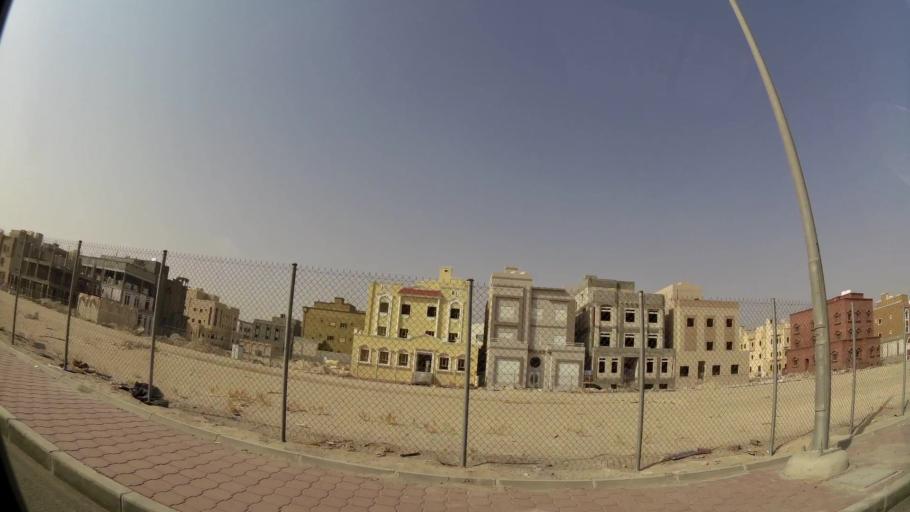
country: KW
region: Muhafazat al Jahra'
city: Al Jahra'
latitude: 29.3552
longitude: 47.7510
